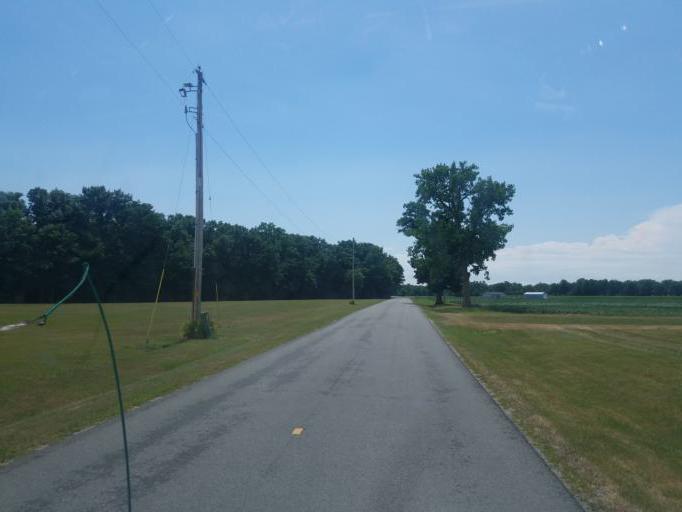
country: US
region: Ohio
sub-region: Paulding County
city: Antwerp
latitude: 41.1820
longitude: -84.7866
